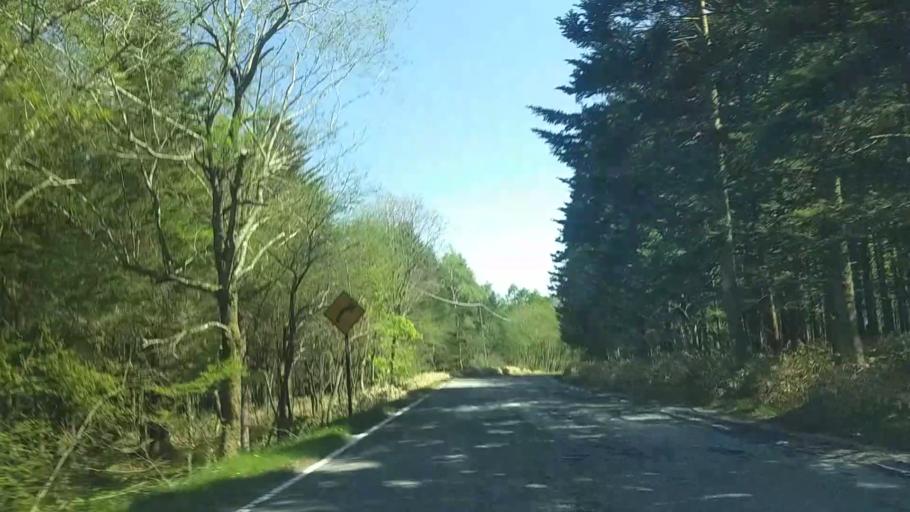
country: JP
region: Yamanashi
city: Nirasaki
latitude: 35.9443
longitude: 138.4196
